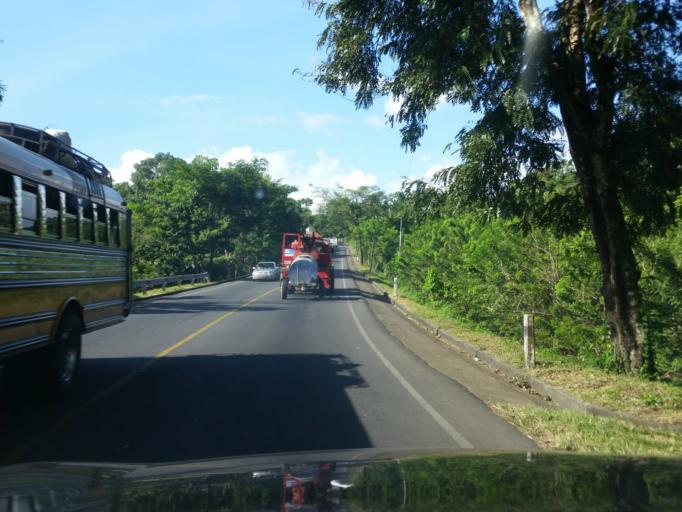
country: NI
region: Granada
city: Diria
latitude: 11.8953
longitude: -86.0639
